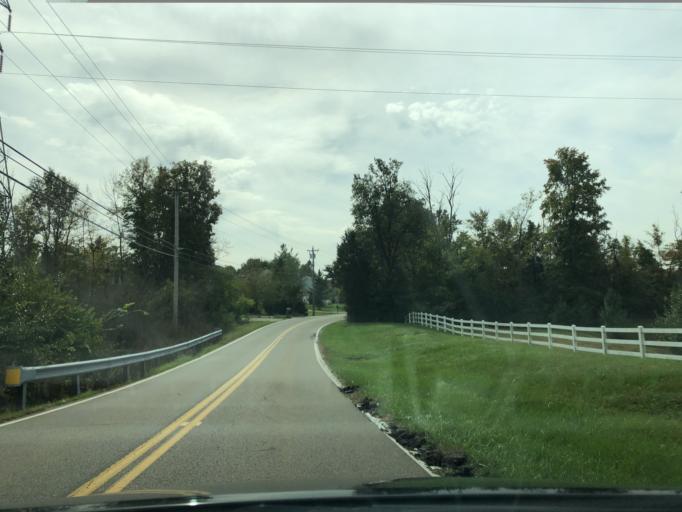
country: US
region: Ohio
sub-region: Hamilton County
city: The Village of Indian Hill
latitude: 39.2316
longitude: -84.2997
